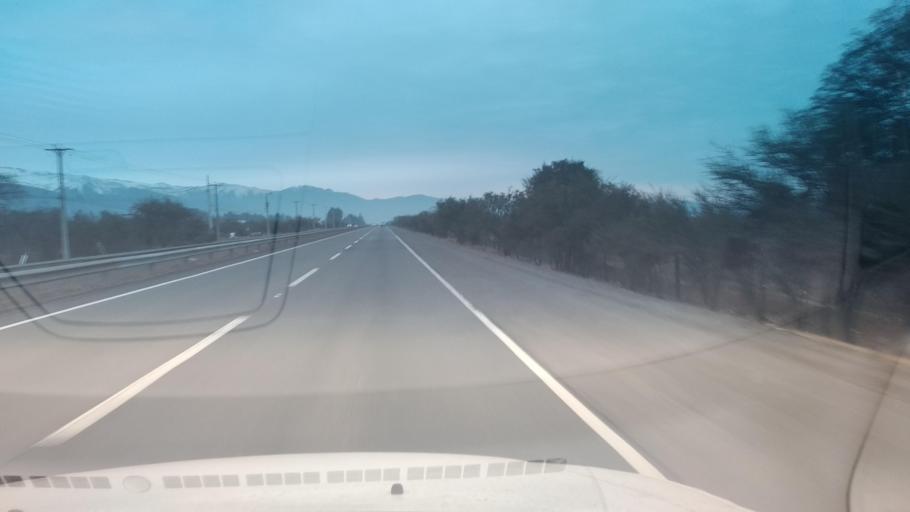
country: CL
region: Santiago Metropolitan
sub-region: Provincia de Chacabuco
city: Chicureo Abajo
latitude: -33.1312
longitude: -70.6703
